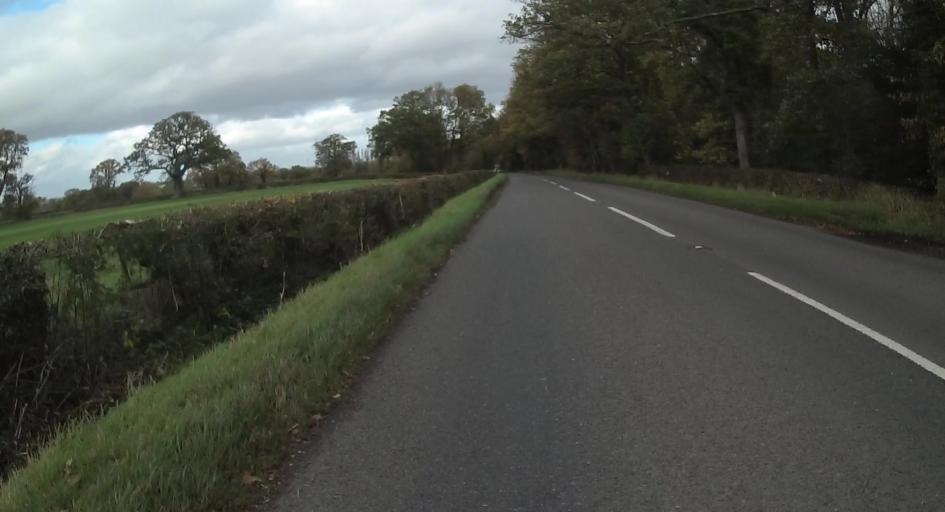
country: GB
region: England
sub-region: Wokingham
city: Swallowfield
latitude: 51.3784
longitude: -0.9948
